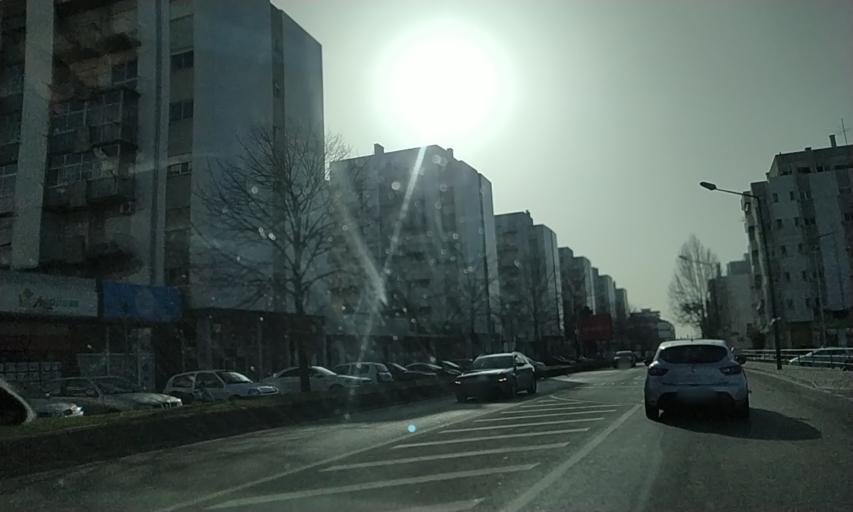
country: PT
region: Leiria
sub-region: Marinha Grande
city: Marinha Grande
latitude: 39.7489
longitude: -8.9250
